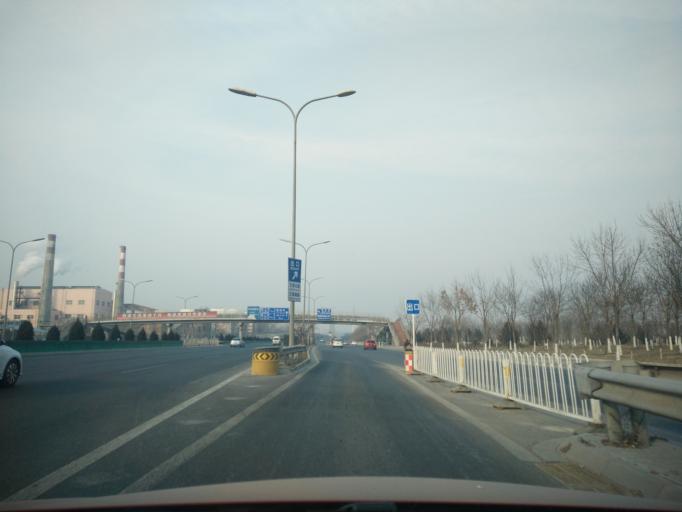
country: CN
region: Beijing
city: Jiugong
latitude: 39.7927
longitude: 116.4240
